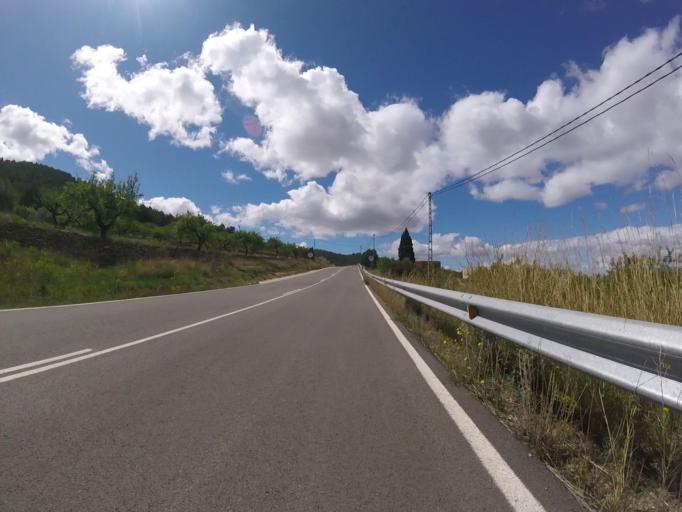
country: ES
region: Valencia
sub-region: Provincia de Castello
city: Culla
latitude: 40.2803
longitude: -0.1121
